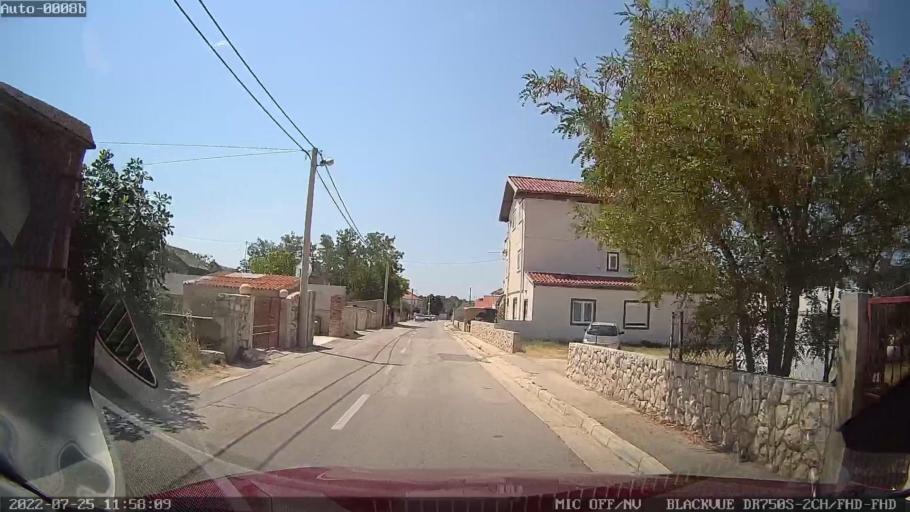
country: HR
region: Zadarska
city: Nin
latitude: 44.2395
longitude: 15.2122
